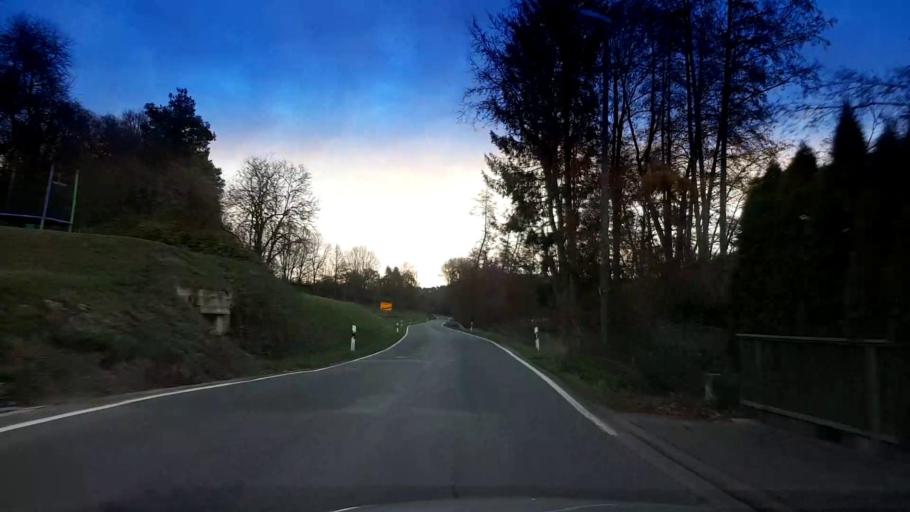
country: DE
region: Bavaria
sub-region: Upper Franconia
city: Walsdorf
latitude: 49.8804
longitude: 10.7618
